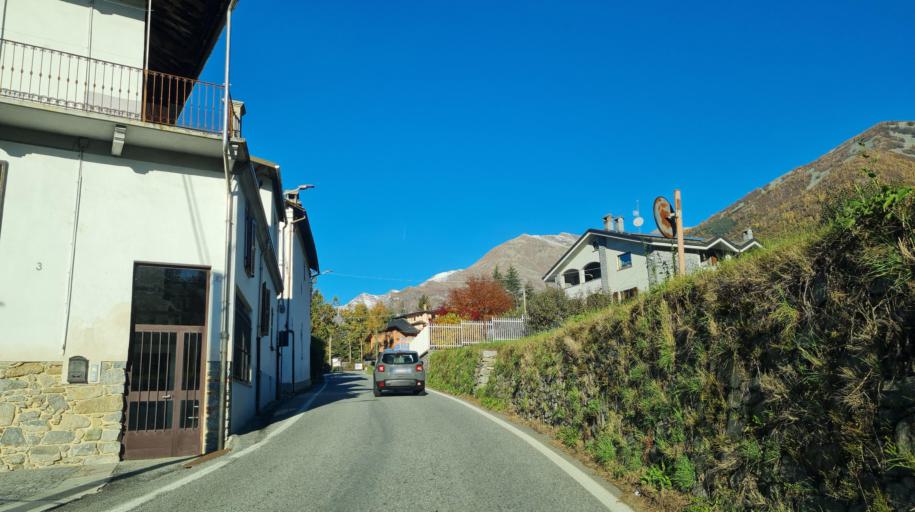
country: IT
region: Piedmont
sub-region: Provincia di Torino
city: Meugliano
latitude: 45.4906
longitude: 7.7796
